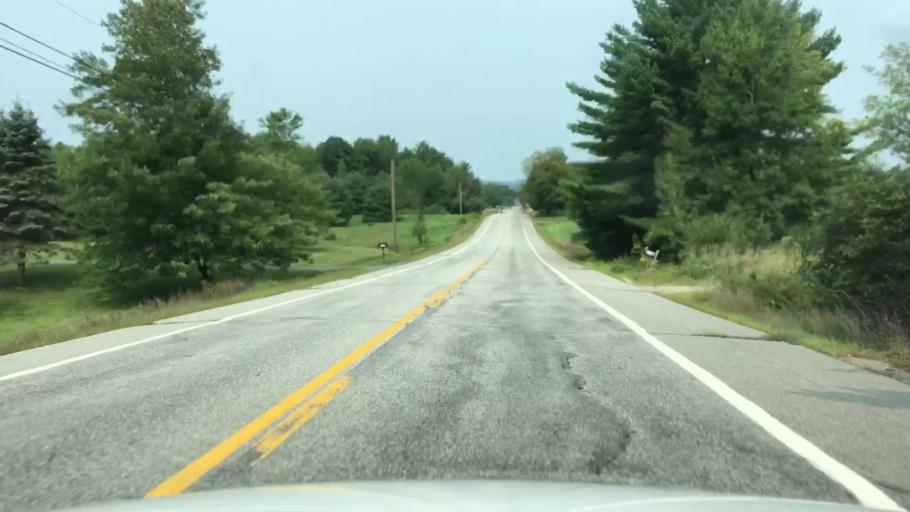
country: US
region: Maine
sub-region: Kennebec County
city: Wayne
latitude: 44.3998
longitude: -70.1241
